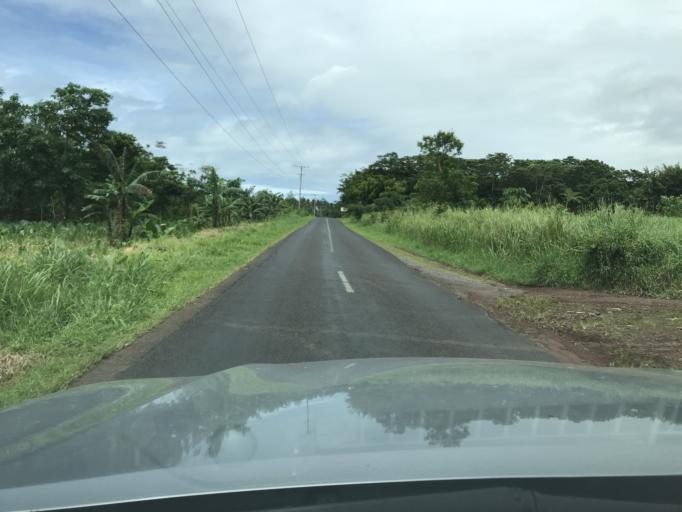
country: WS
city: Nofoali`i
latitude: -13.8740
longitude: -171.9263
